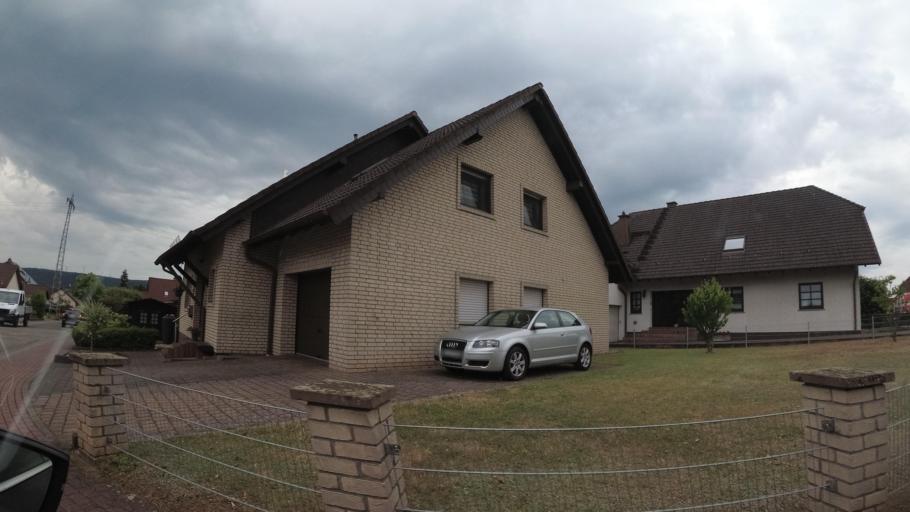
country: DE
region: Rheinland-Pfalz
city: Hutschenhausen
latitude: 49.4235
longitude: 7.4879
